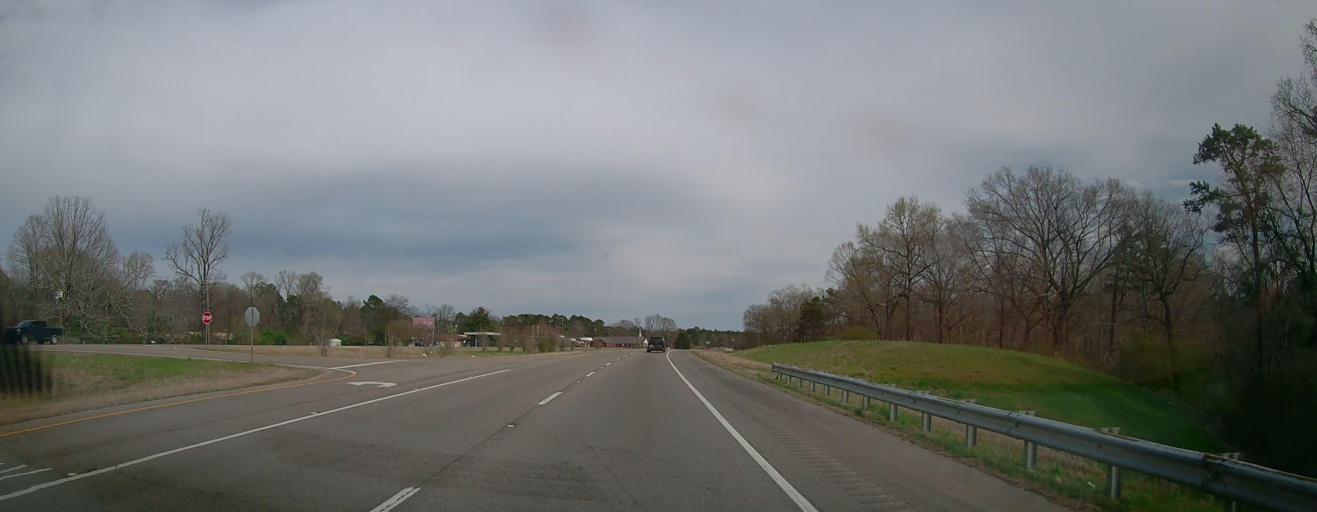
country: US
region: Alabama
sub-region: Walker County
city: Cordova
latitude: 33.8024
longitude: -87.1207
